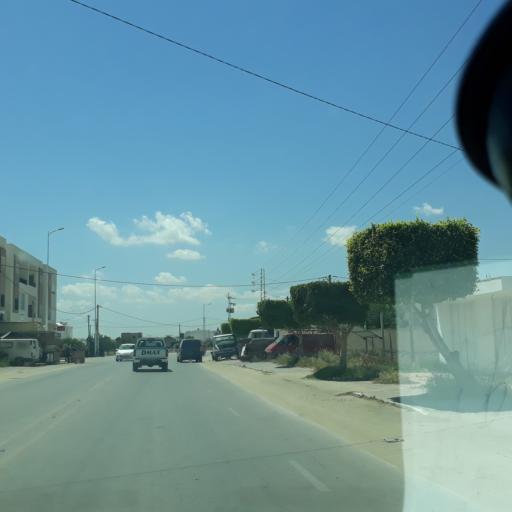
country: TN
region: Safaqis
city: Sfax
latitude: 34.8158
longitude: 10.7424
